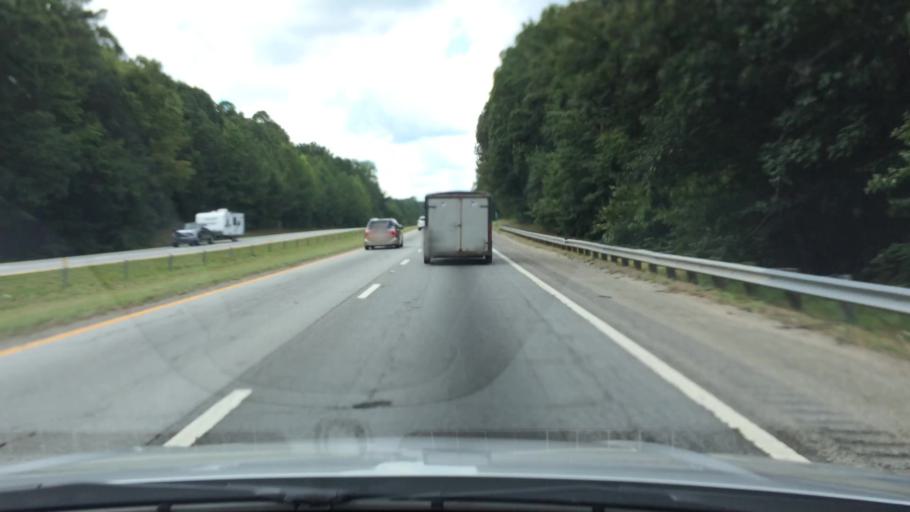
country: US
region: South Carolina
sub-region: Lexington County
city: Chapin
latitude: 34.2099
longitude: -81.3835
